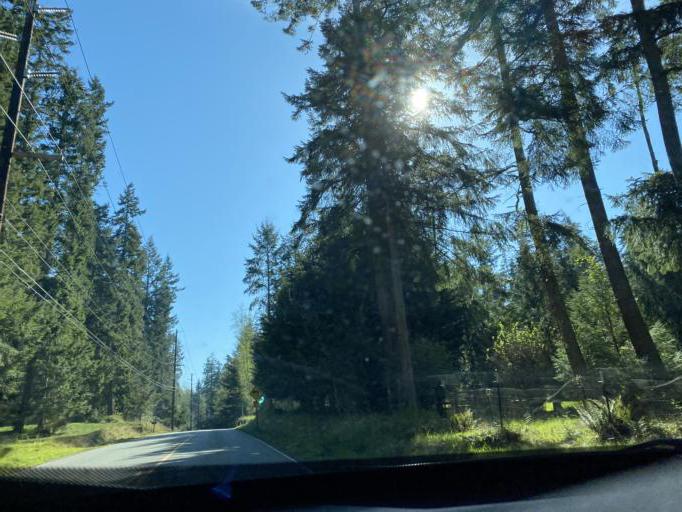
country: US
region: Washington
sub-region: Island County
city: Freeland
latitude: 48.0799
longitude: -122.5869
